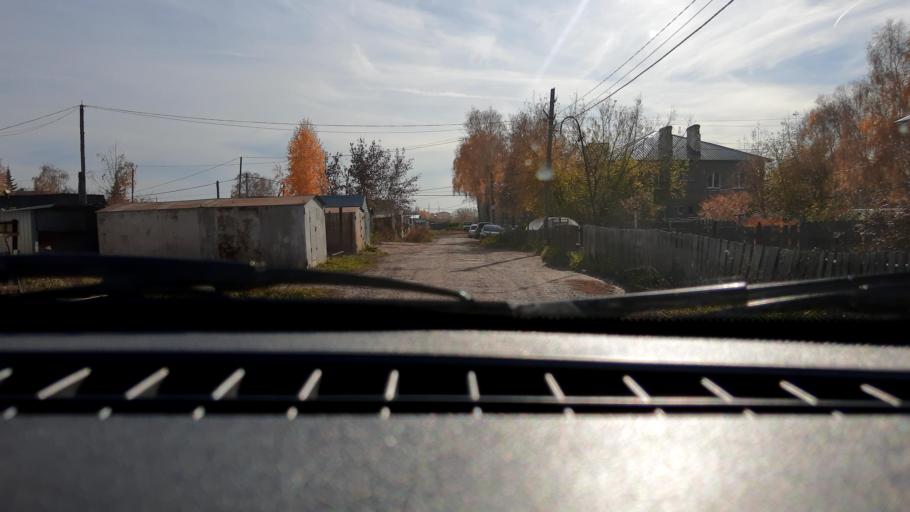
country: RU
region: Bashkortostan
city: Mikhaylovka
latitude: 54.8011
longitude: 55.8871
